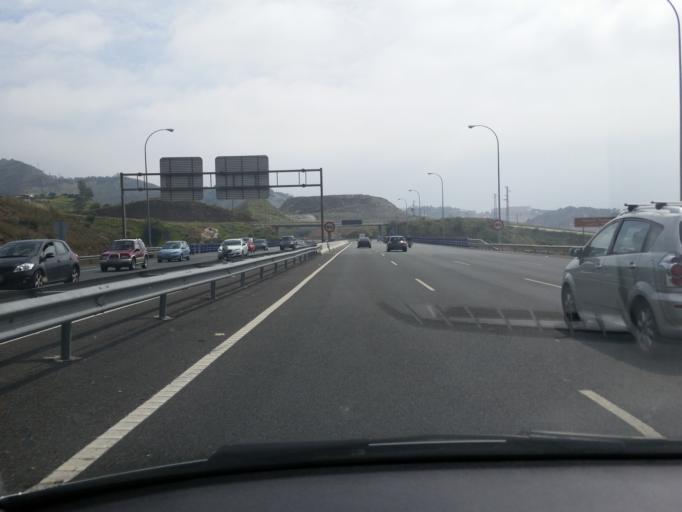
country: ES
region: Andalusia
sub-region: Provincia de Malaga
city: Malaga
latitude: 36.7419
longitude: -4.4032
